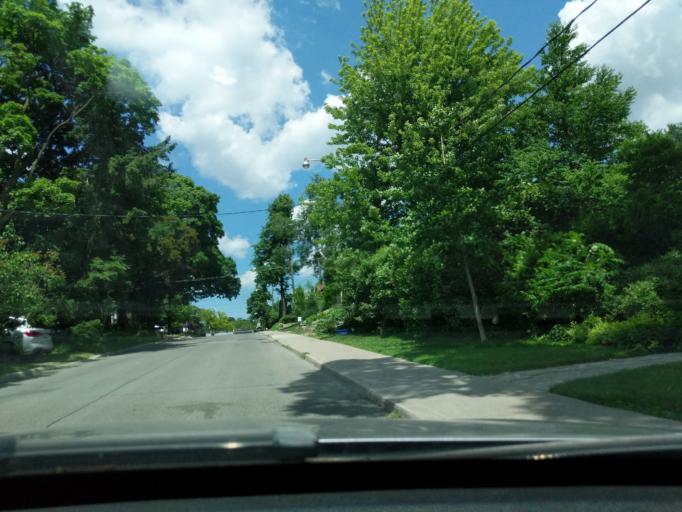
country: CA
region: Ontario
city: Toronto
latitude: 43.7023
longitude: -79.4113
